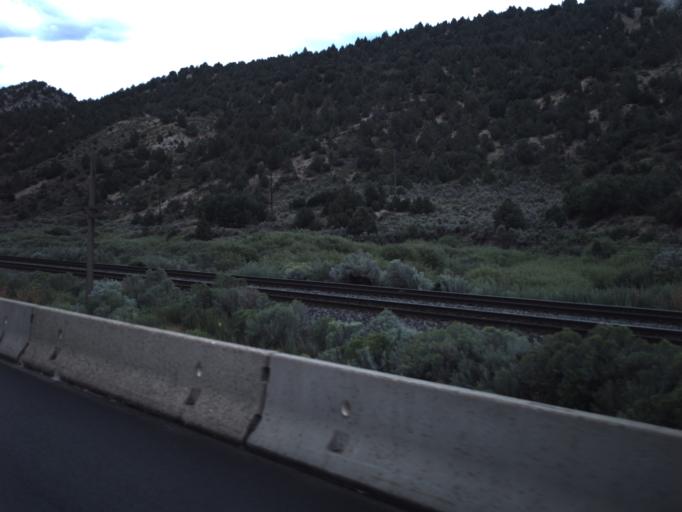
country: US
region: Utah
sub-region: Utah County
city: Mapleton
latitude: 39.9517
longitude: -111.2781
